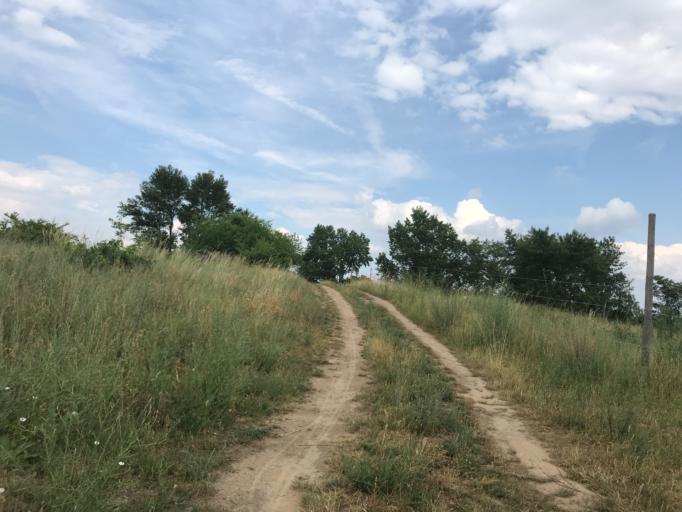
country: DE
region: Rheinland-Pfalz
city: Budenheim
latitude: 50.0025
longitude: 8.1809
